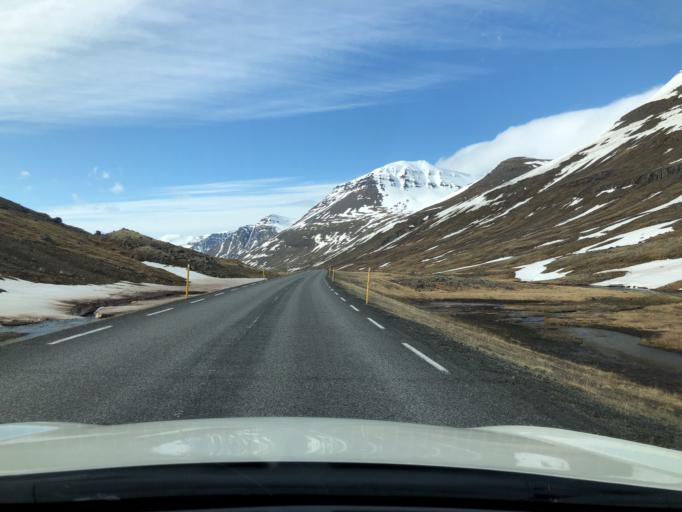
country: IS
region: East
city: Reydarfjoerdur
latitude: 65.0887
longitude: -14.3314
